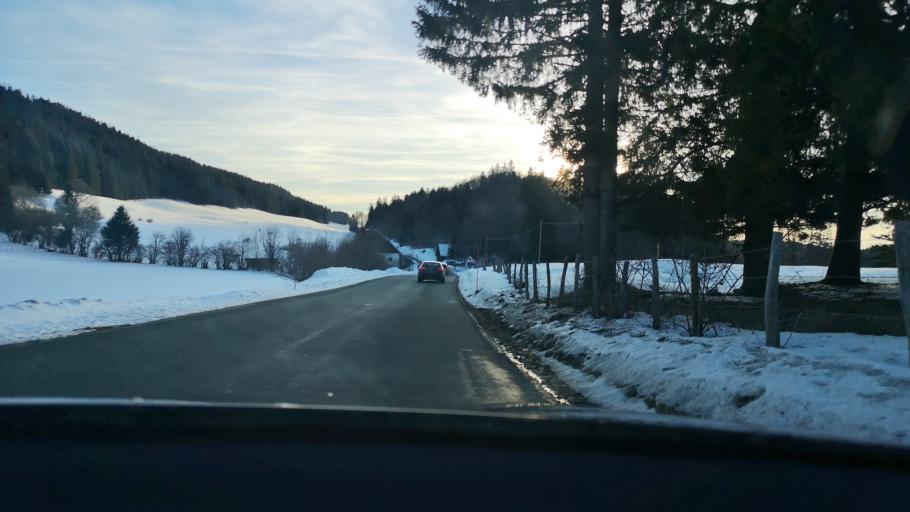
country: FR
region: Franche-Comte
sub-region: Departement du Doubs
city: Gilley
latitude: 46.9823
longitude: 6.5011
